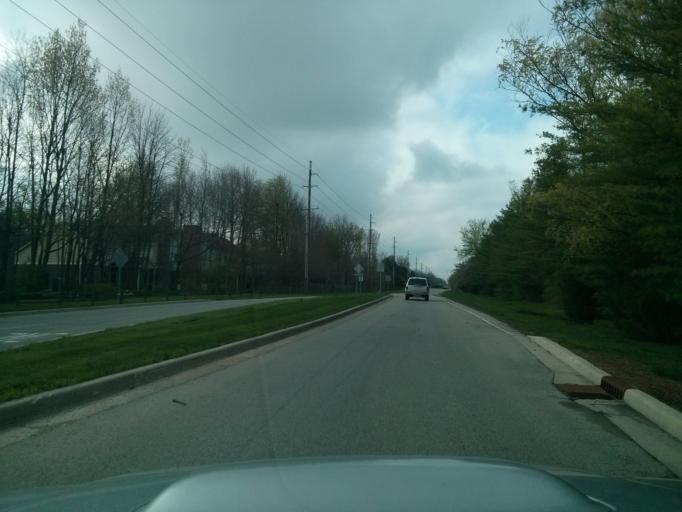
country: US
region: Indiana
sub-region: Hamilton County
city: Carmel
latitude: 39.9776
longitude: -86.1650
